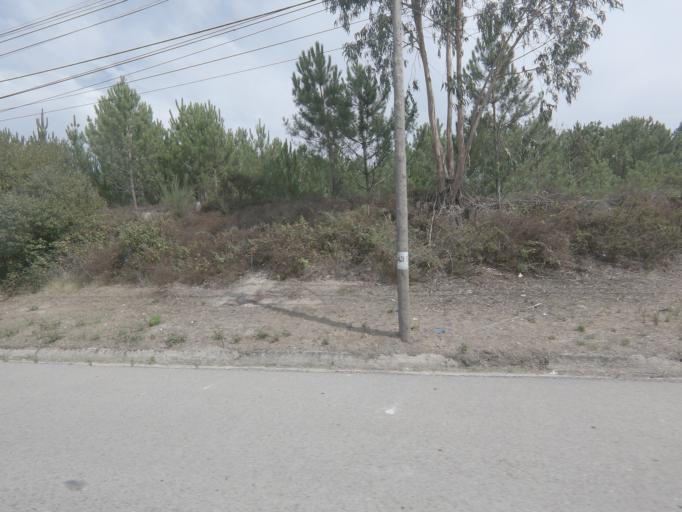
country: PT
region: Leiria
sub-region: Leiria
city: Caranguejeira
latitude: 39.8305
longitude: -8.7207
